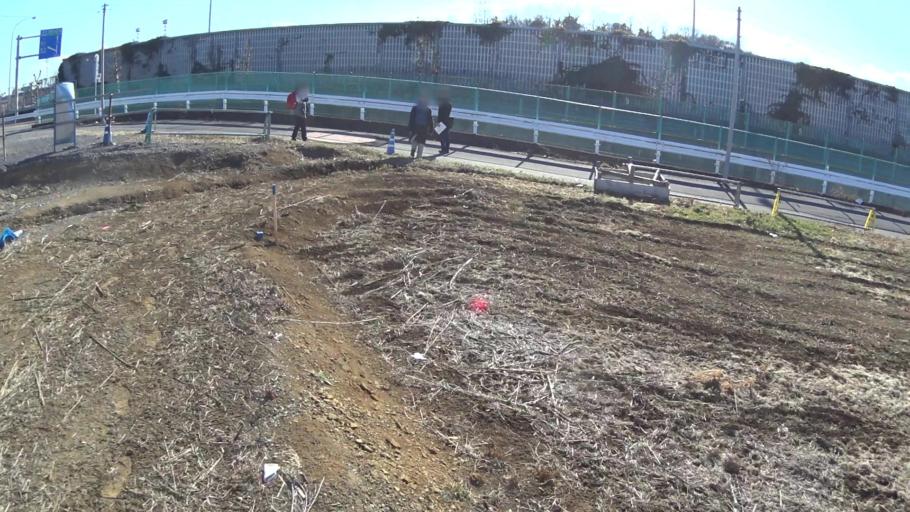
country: JP
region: Saitama
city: Saitama
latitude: 35.8957
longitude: 139.7194
